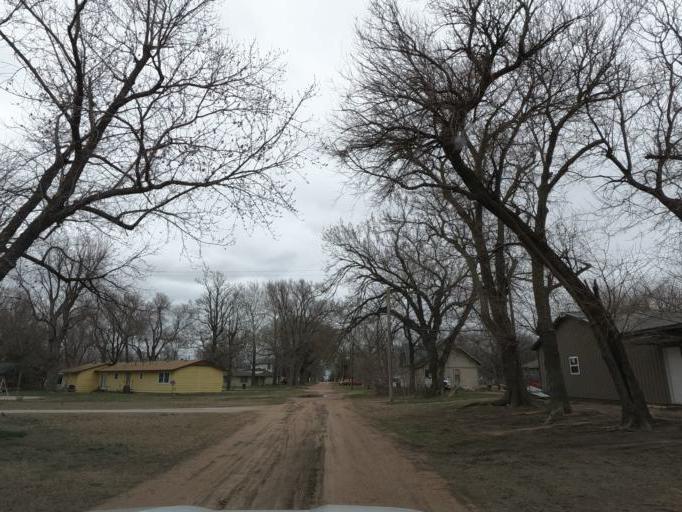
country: US
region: Kansas
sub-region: Stafford County
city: Stafford
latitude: 37.9573
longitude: -98.4119
